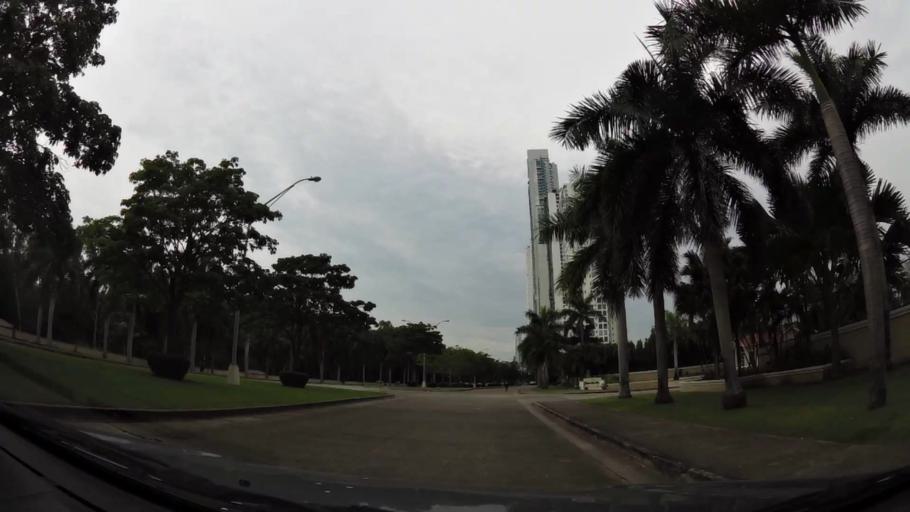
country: PA
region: Panama
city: San Miguelito
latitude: 9.0108
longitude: -79.4595
